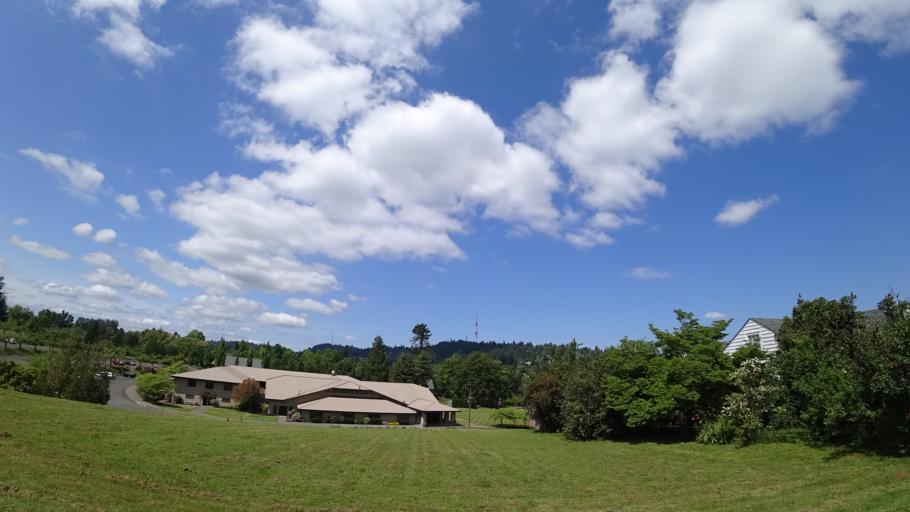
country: US
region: Oregon
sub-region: Multnomah County
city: Portland
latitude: 45.4724
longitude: -122.6999
